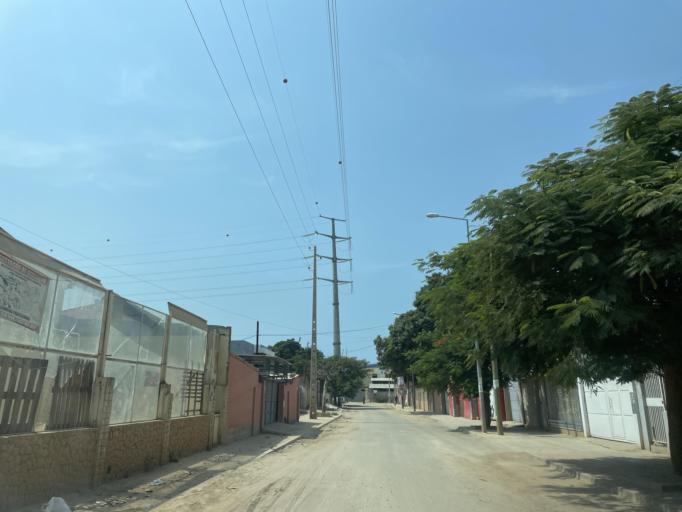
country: AO
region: Luanda
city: Luanda
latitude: -8.9021
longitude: 13.1827
